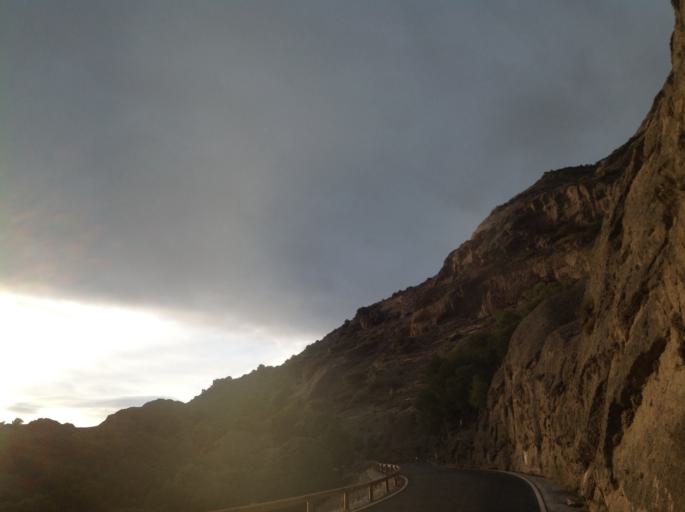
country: ES
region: Andalusia
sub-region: Provincia de Malaga
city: Carratraca
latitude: 36.9128
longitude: -4.7874
